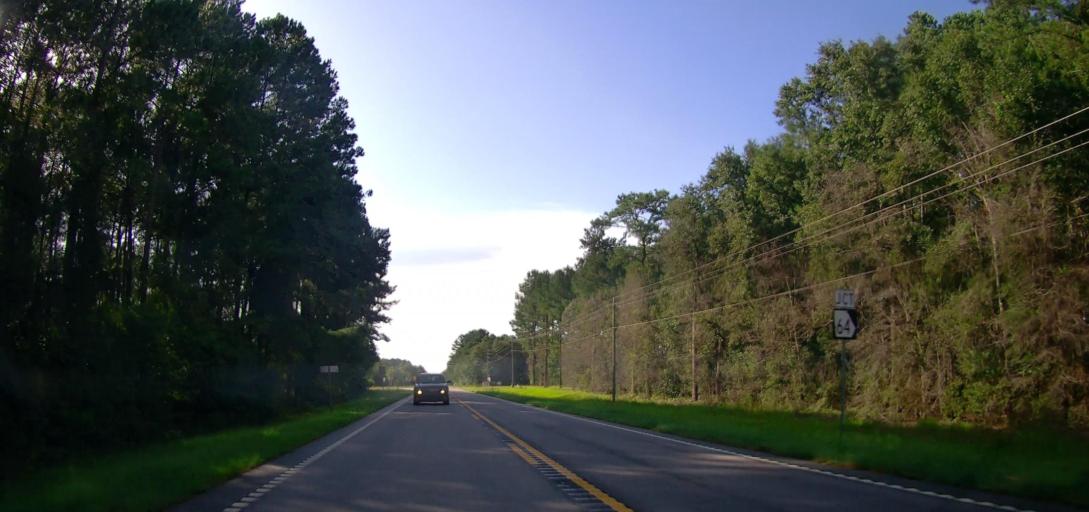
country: US
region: Georgia
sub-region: Coffee County
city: Nicholls
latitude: 31.4088
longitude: -82.6800
